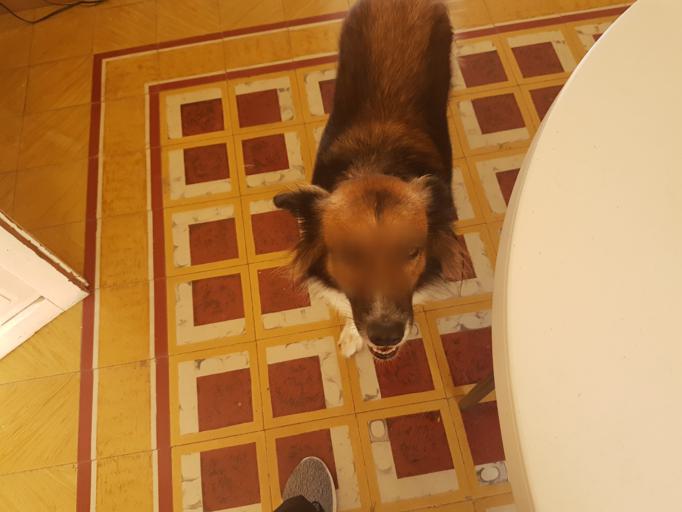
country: MX
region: Yucatan
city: Merida
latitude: 20.9833
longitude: -89.6302
